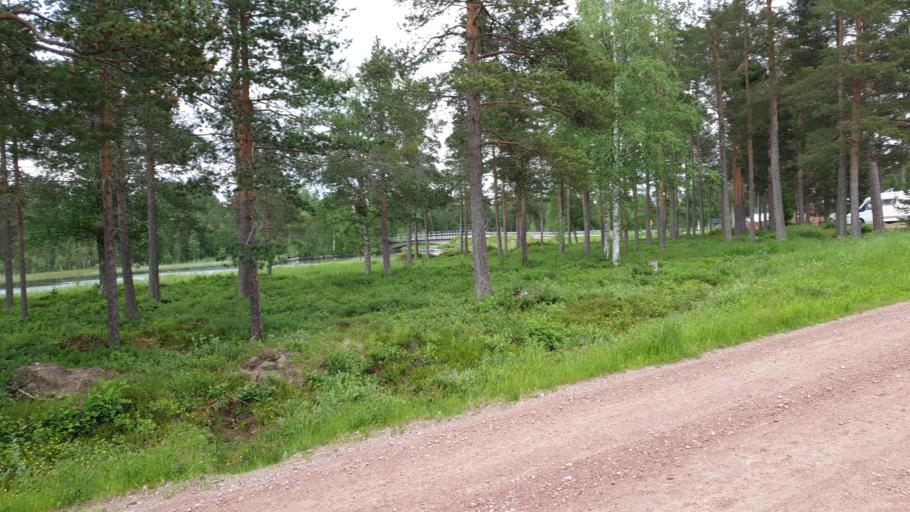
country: SE
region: Jaemtland
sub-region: Harjedalens Kommun
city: Sveg
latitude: 61.7970
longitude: 14.6340
